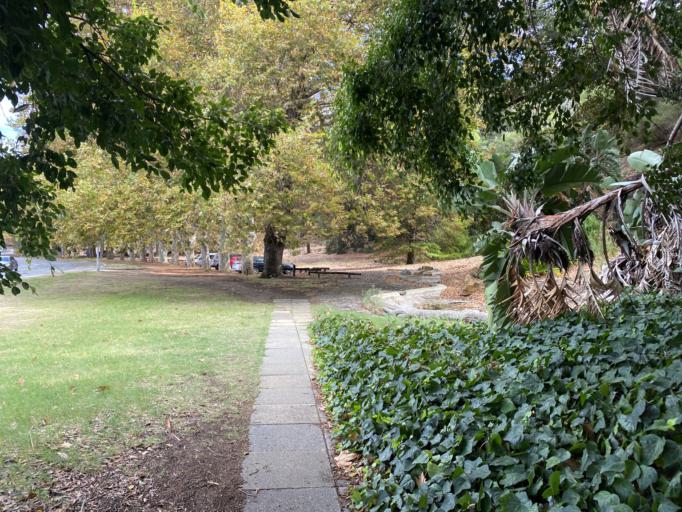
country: AU
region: Western Australia
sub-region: City of Perth
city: West Perth
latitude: -31.9628
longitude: 115.8428
